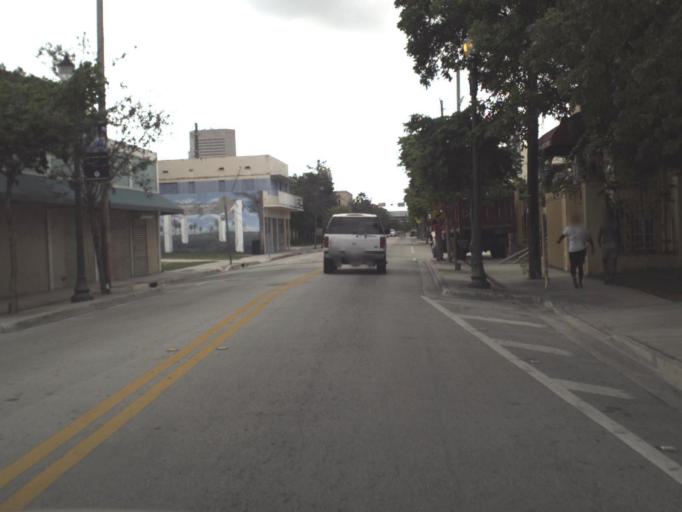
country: US
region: Florida
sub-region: Miami-Dade County
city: Miami
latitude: 25.7877
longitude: -80.1999
